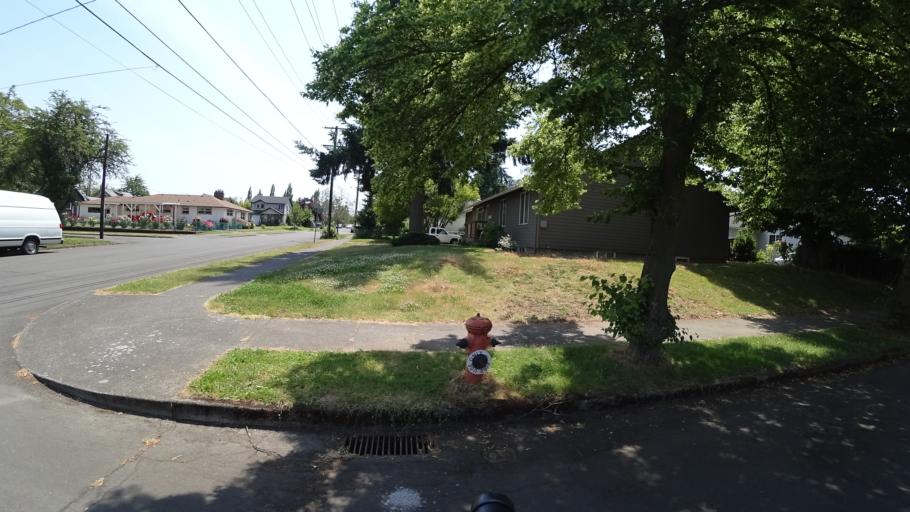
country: US
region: Oregon
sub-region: Multnomah County
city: Portland
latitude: 45.5805
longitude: -122.6925
